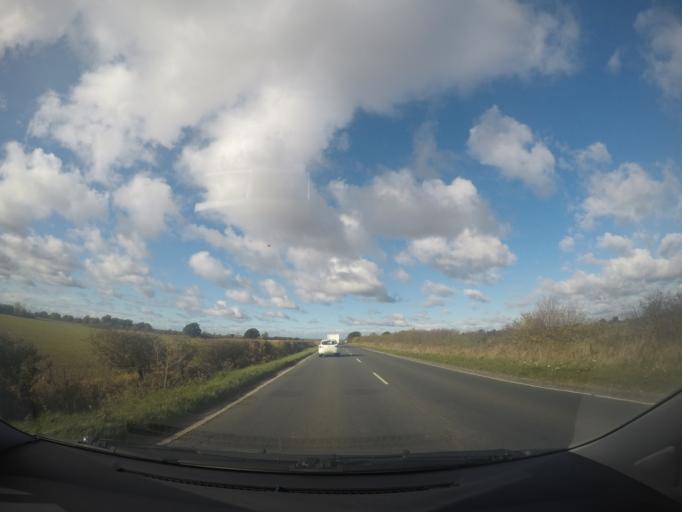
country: GB
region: England
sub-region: City of York
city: Nether Poppleton
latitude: 53.9833
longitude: -1.2096
